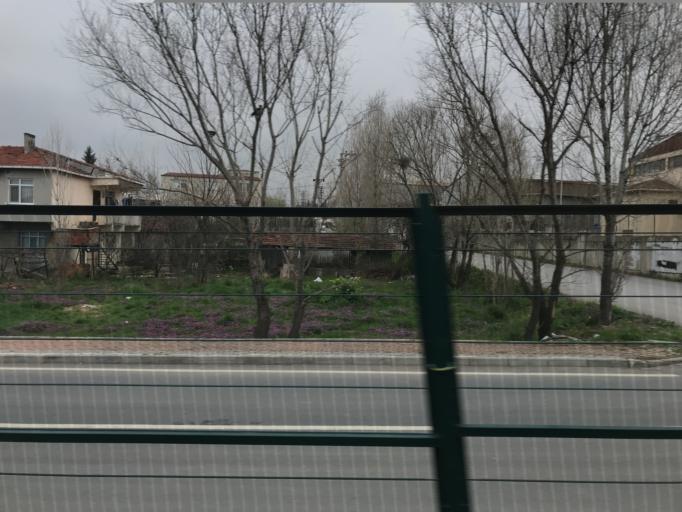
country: TR
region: Kocaeli
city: Darica
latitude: 40.7892
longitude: 29.3954
